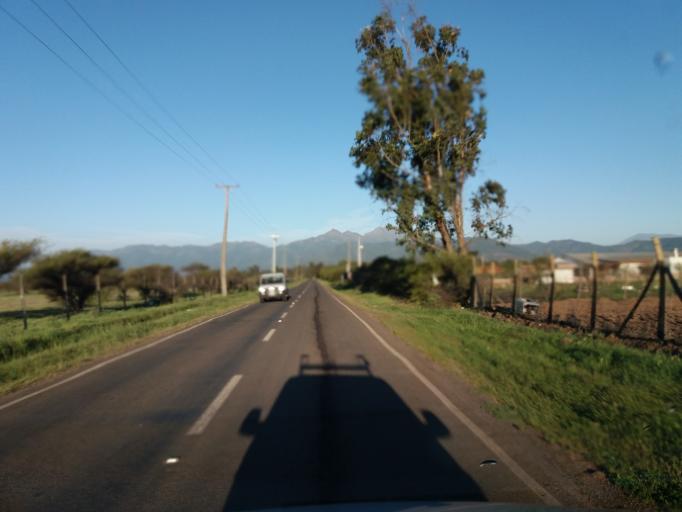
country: CL
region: Valparaiso
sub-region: Provincia de Quillota
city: Quillota
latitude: -32.9168
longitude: -71.3278
